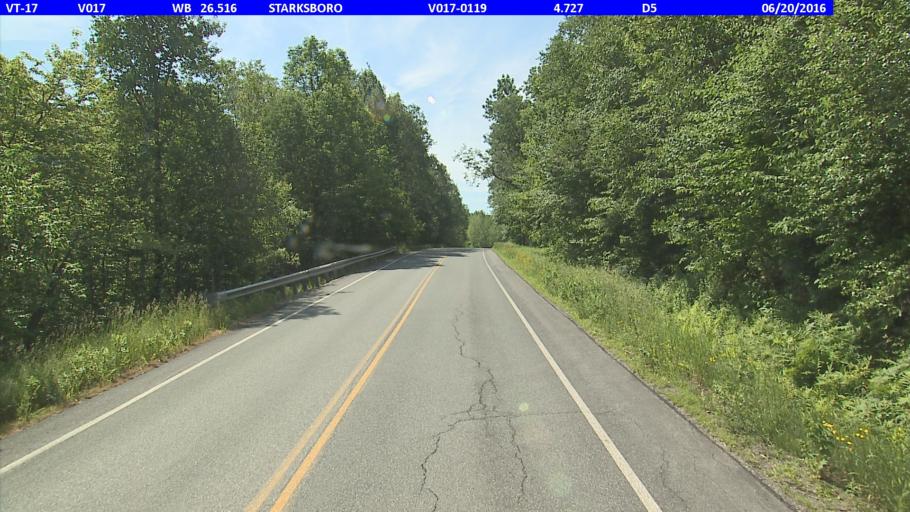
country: US
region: Vermont
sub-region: Addison County
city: Bristol
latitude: 44.2072
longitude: -72.9653
